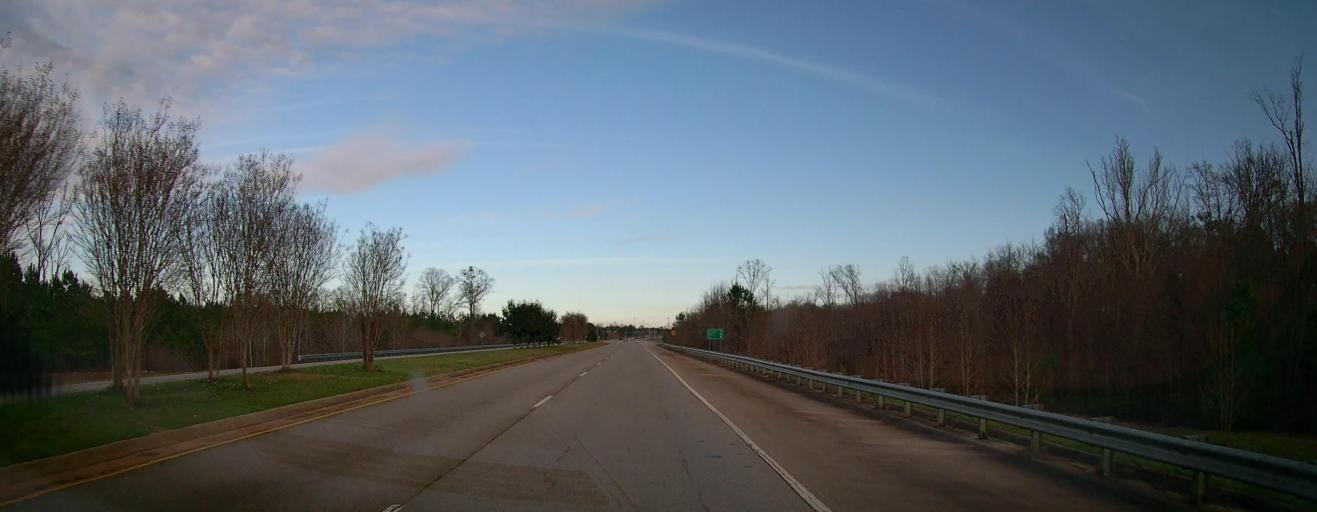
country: US
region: Georgia
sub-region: Troup County
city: West Point
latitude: 32.9314
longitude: -85.1230
